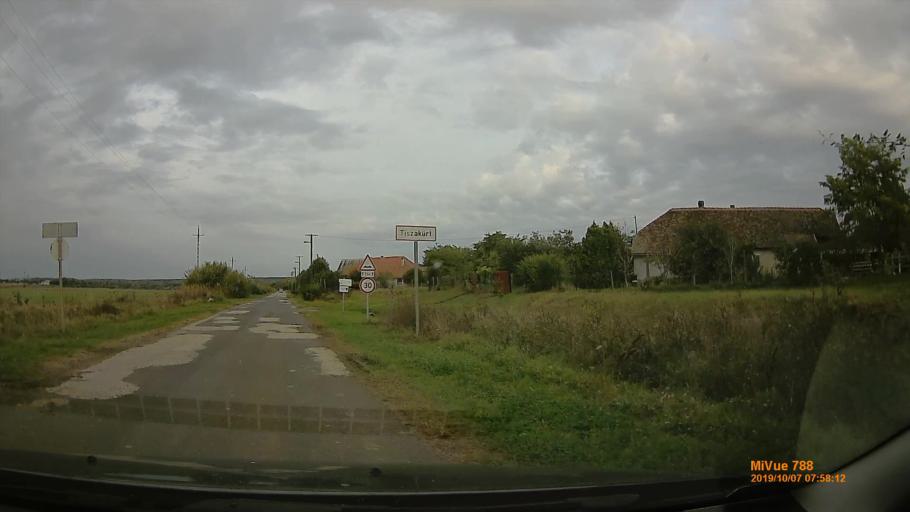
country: HU
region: Jasz-Nagykun-Szolnok
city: Cserkeszolo
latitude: 46.8823
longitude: 20.1355
